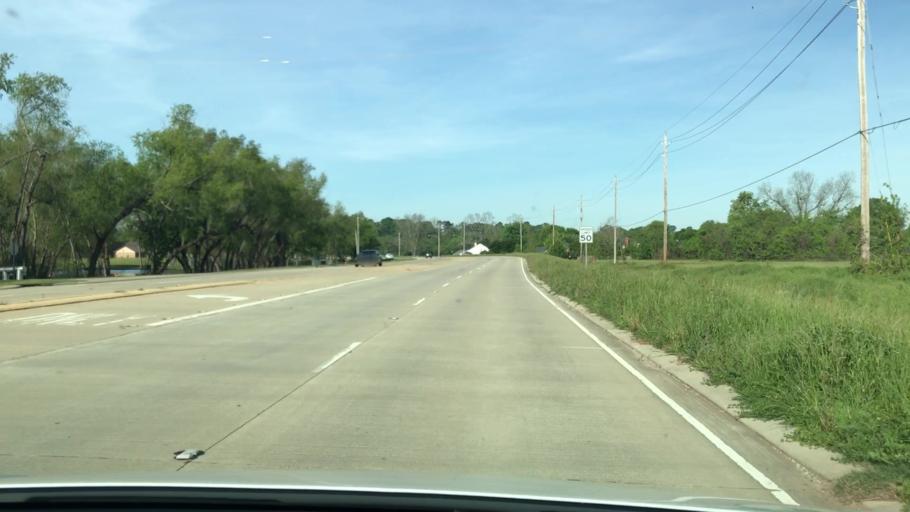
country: US
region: Louisiana
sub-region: Bossier Parish
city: Bossier City
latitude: 32.4002
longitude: -93.7172
